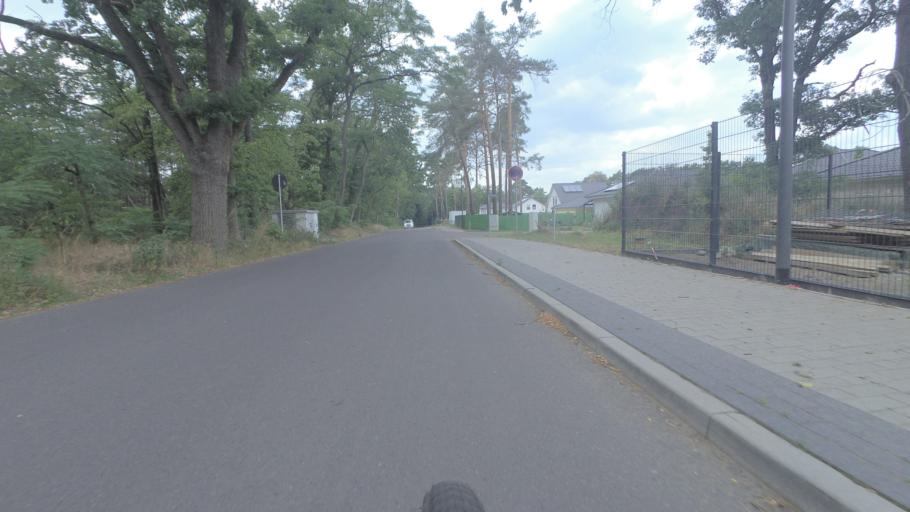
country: DE
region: Brandenburg
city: Zossen
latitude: 52.1890
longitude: 13.4726
